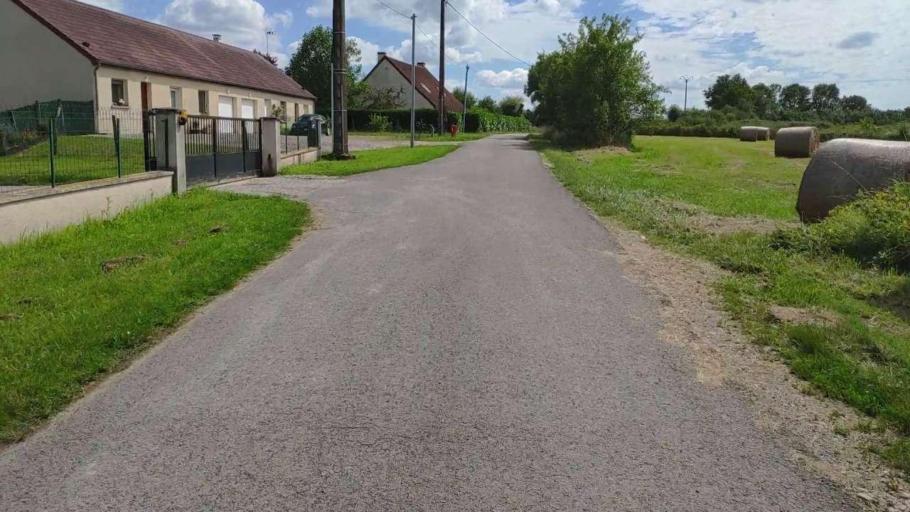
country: FR
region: Franche-Comte
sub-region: Departement du Jura
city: Bletterans
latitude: 46.8279
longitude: 5.4502
